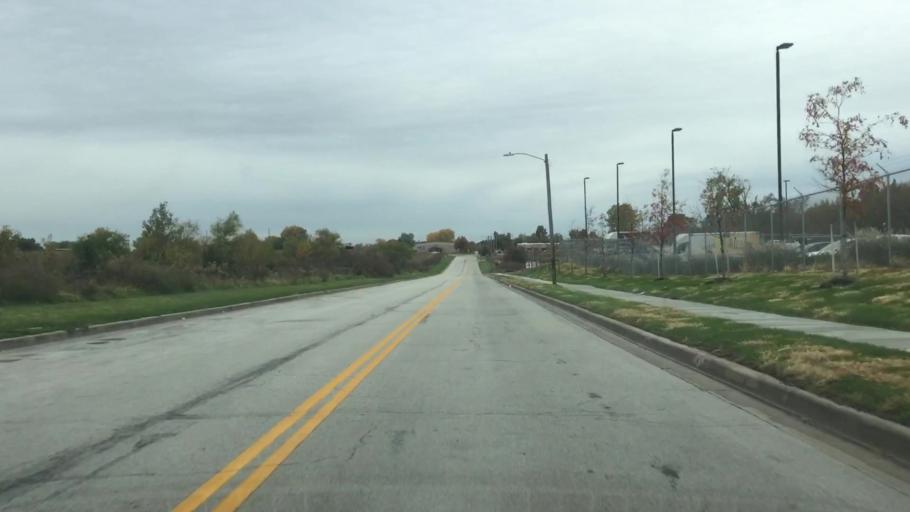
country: US
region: Missouri
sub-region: Jackson County
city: Lees Summit
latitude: 38.8885
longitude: -94.3676
